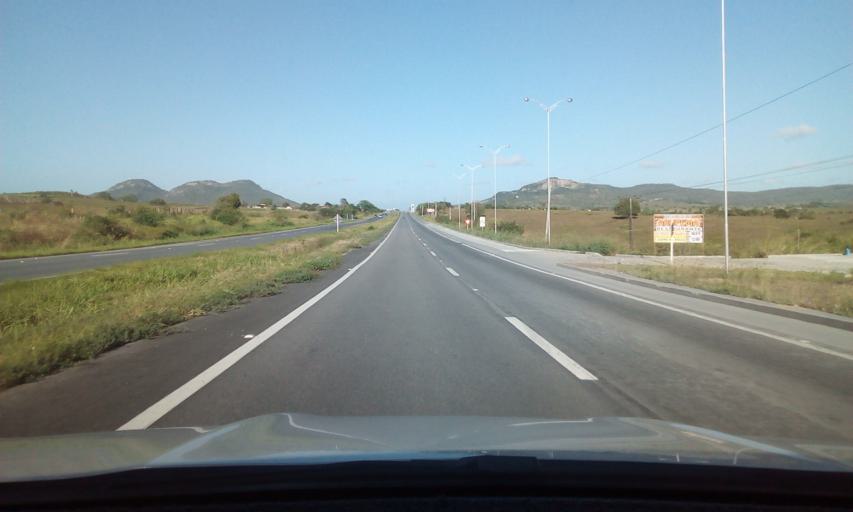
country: BR
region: Paraiba
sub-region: Gurinhem
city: Gurinhem
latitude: -7.1669
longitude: -35.3635
